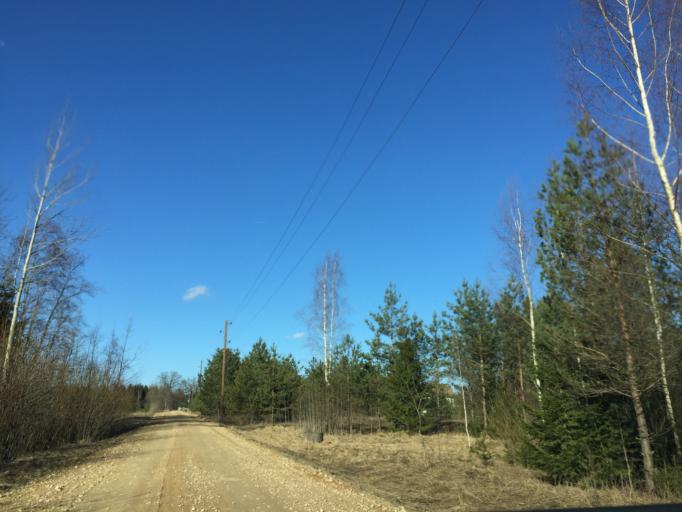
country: LV
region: Ogre
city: Ogre
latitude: 56.8780
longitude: 24.7098
